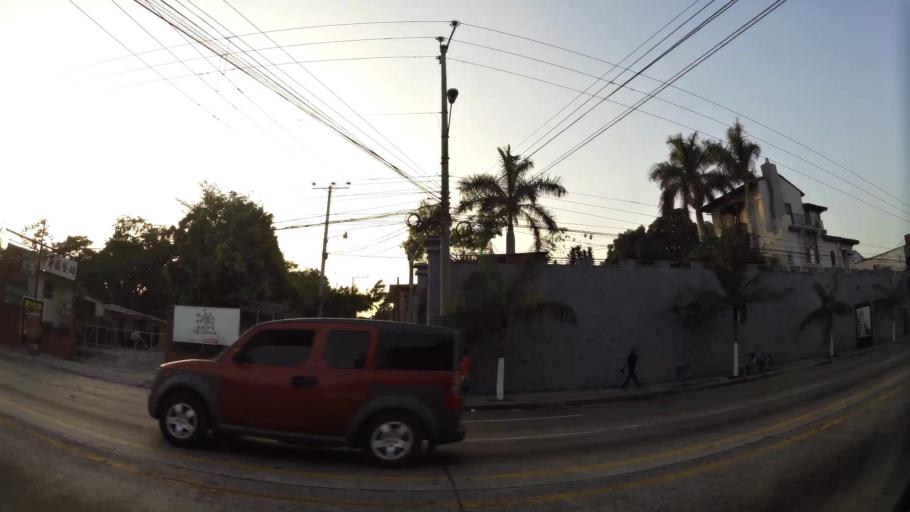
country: SV
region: San Salvador
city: San Salvador
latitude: 13.6998
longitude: -89.2162
